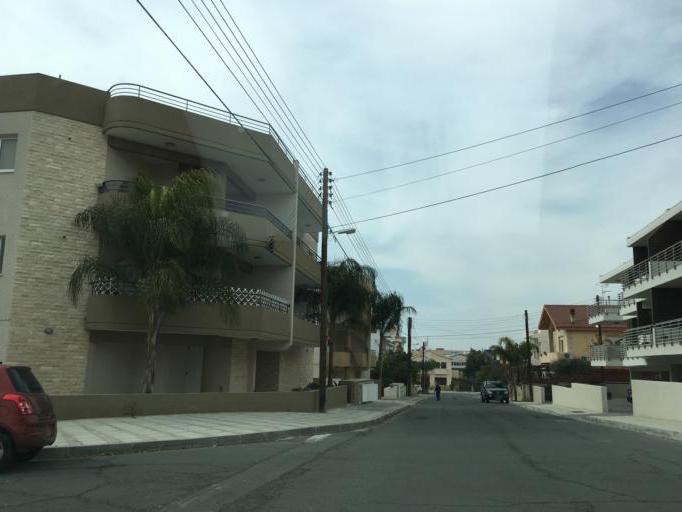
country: CY
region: Limassol
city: Mouttagiaka
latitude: 34.7063
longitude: 33.0773
